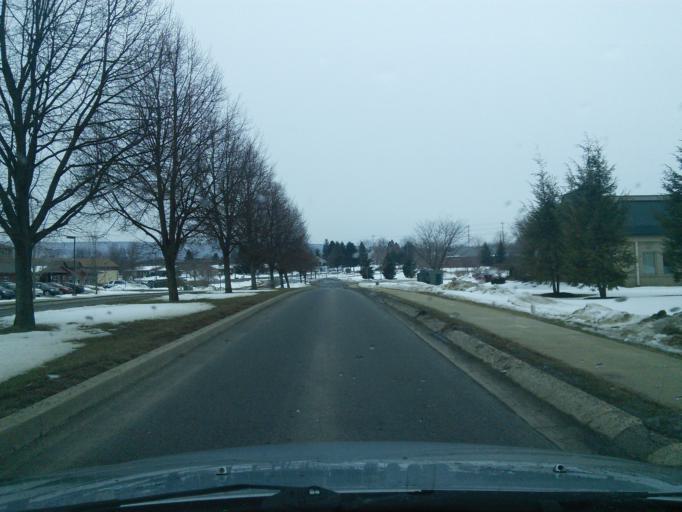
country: US
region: Pennsylvania
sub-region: Centre County
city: State College
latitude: 40.7683
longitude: -77.8827
